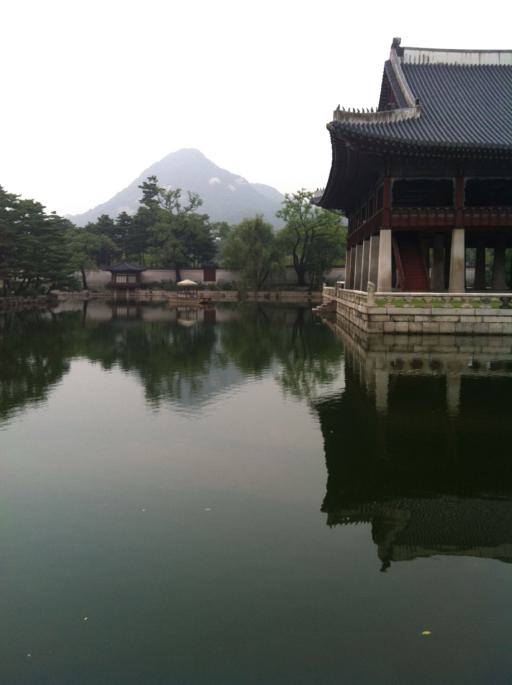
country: KR
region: Seoul
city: Seoul
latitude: 37.5792
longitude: 126.9758
